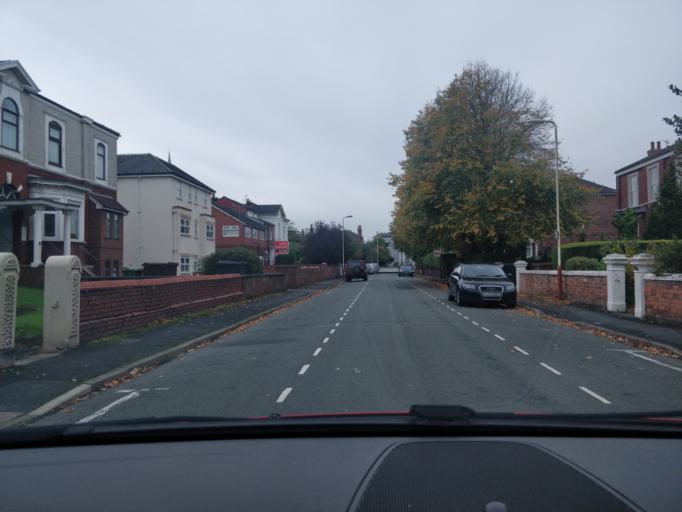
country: GB
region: England
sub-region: Sefton
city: Southport
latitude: 53.6487
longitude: -2.9945
